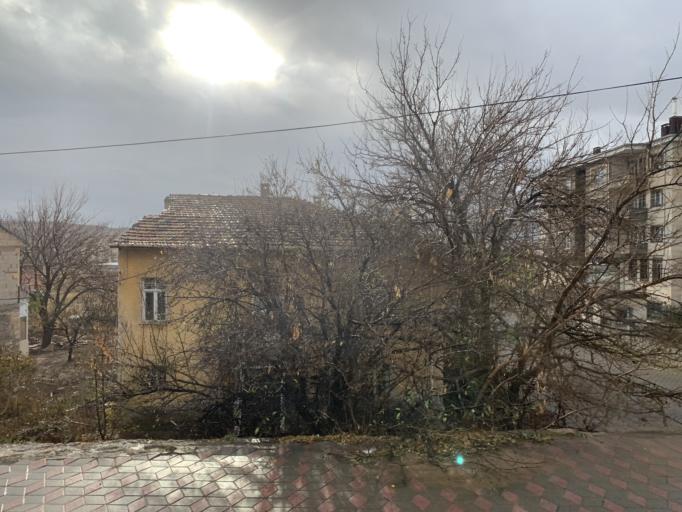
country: TR
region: Nevsehir
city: Avanos
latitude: 38.7203
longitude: 34.8524
